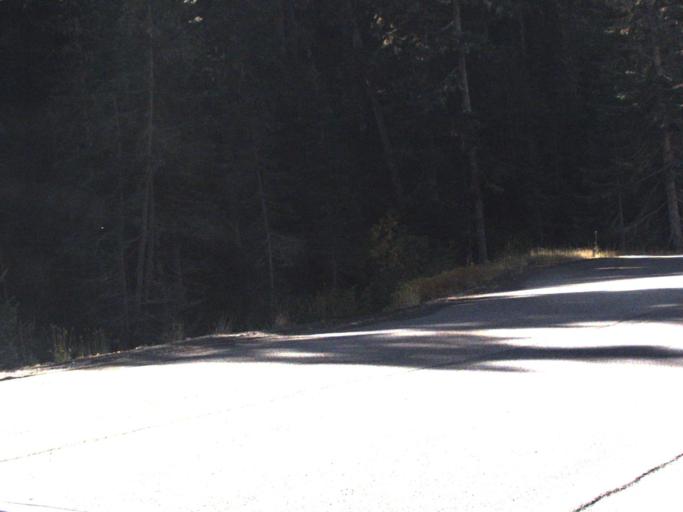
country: US
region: Washington
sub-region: Yakima County
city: Tieton
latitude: 46.6275
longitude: -121.4238
